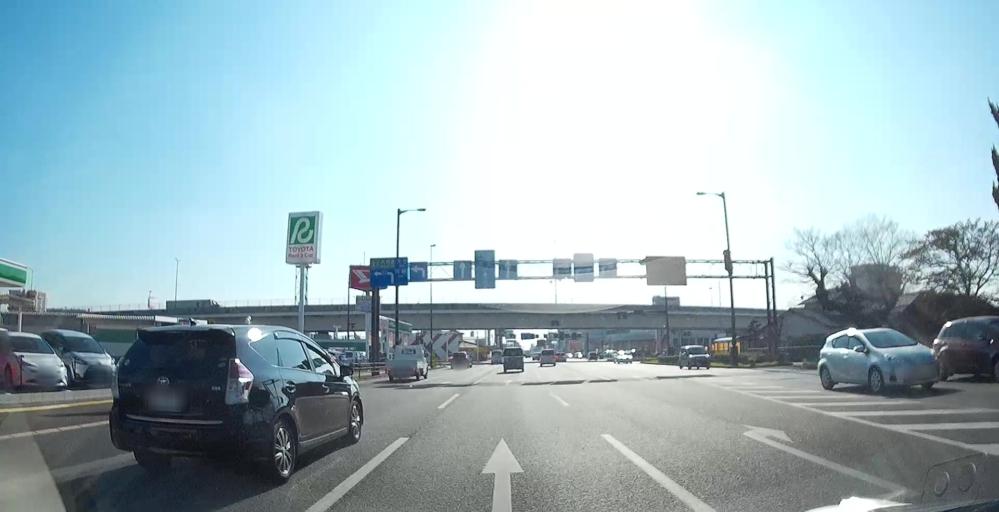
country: JP
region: Kumamoto
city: Kumamoto
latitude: 32.7632
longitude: 130.6899
